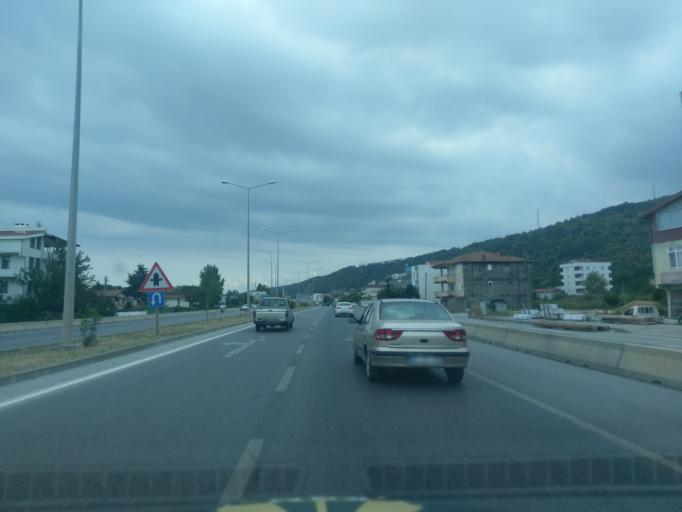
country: TR
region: Samsun
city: Taflan
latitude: 41.3929
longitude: 36.2005
